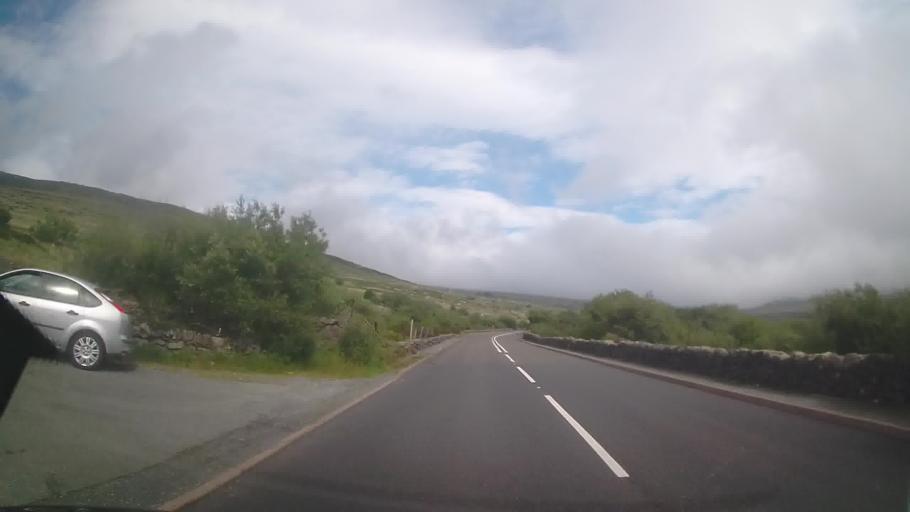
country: GB
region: Wales
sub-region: Gwynedd
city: Aber
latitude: 53.1233
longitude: -3.9626
